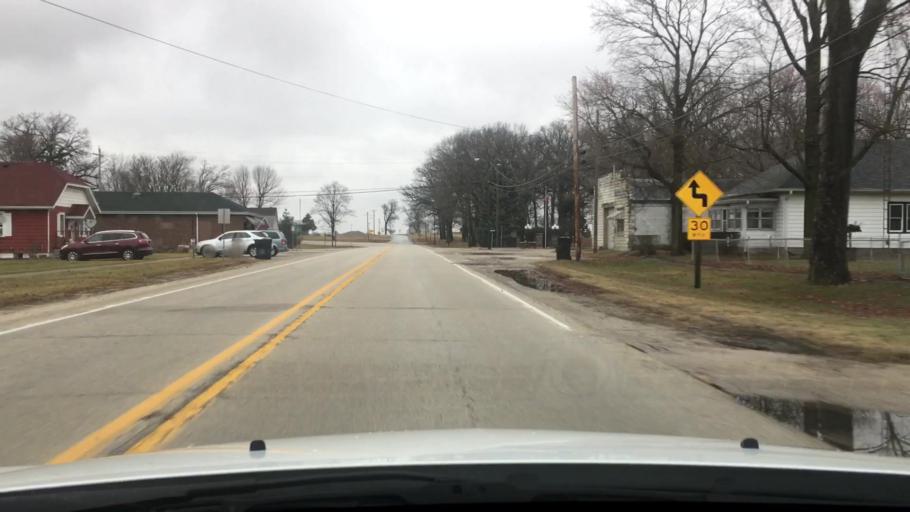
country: US
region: Illinois
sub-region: Iroquois County
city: Sheldon
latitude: 40.8266
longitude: -87.5816
